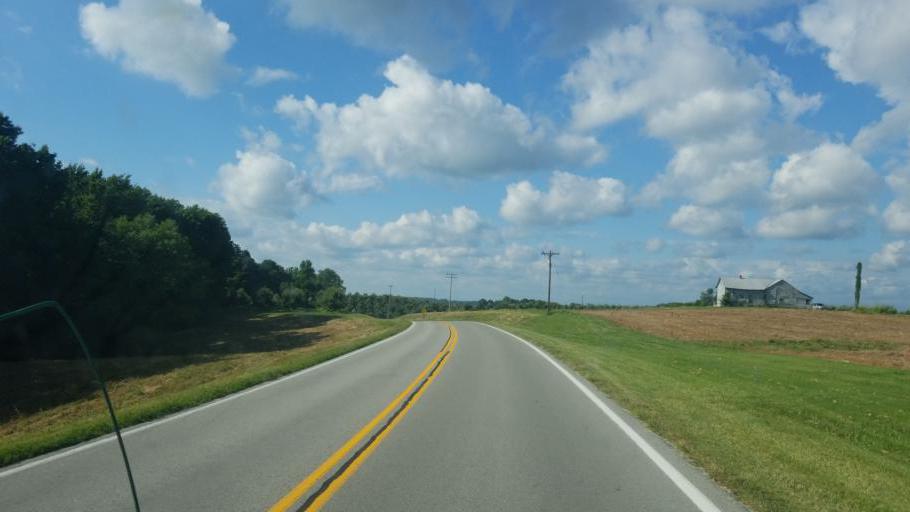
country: US
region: Illinois
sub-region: Union County
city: Cobden
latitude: 37.5960
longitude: -89.3217
